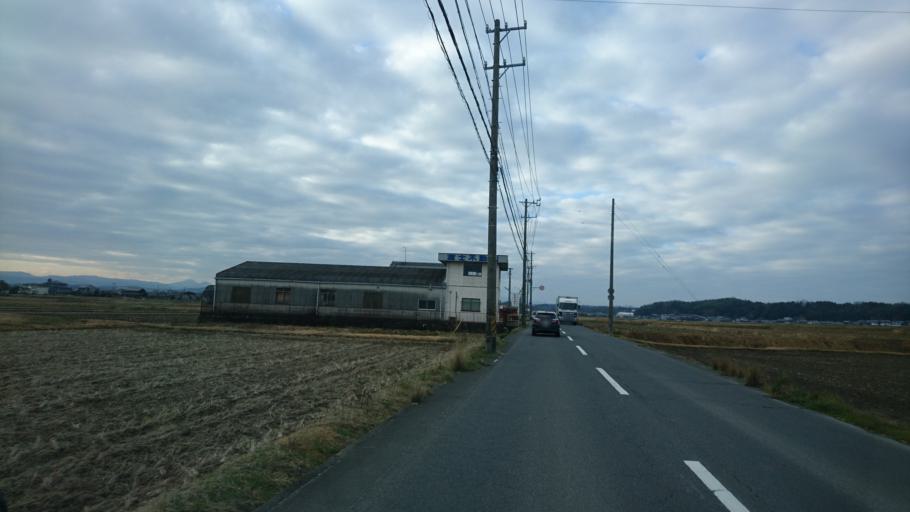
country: JP
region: Mie
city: Ueno-ebisumachi
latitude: 34.7514
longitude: 136.1106
